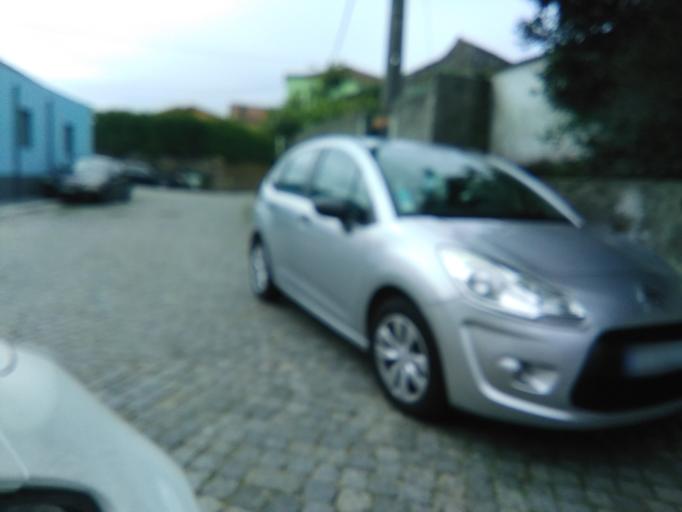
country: PT
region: Porto
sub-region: Matosinhos
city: Lavra
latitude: 41.2345
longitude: -8.7160
